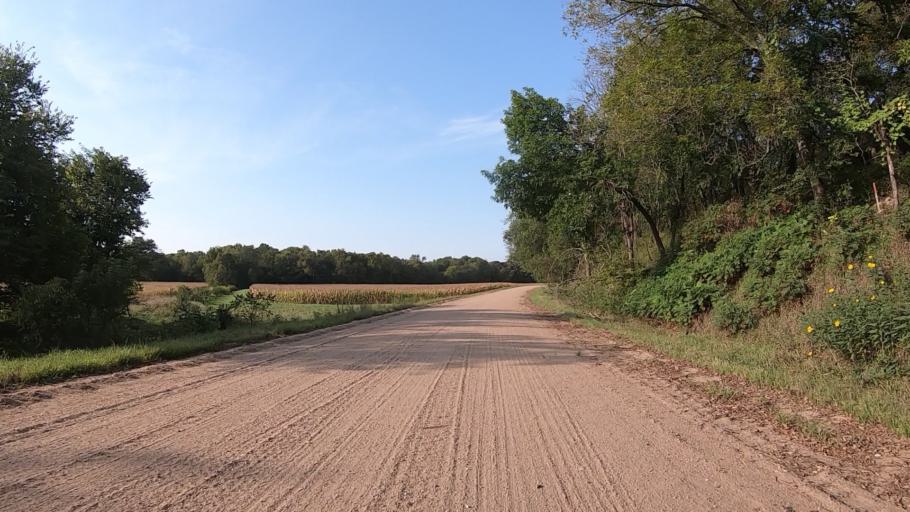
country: US
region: Kansas
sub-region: Marshall County
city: Blue Rapids
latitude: 39.6641
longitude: -96.8157
